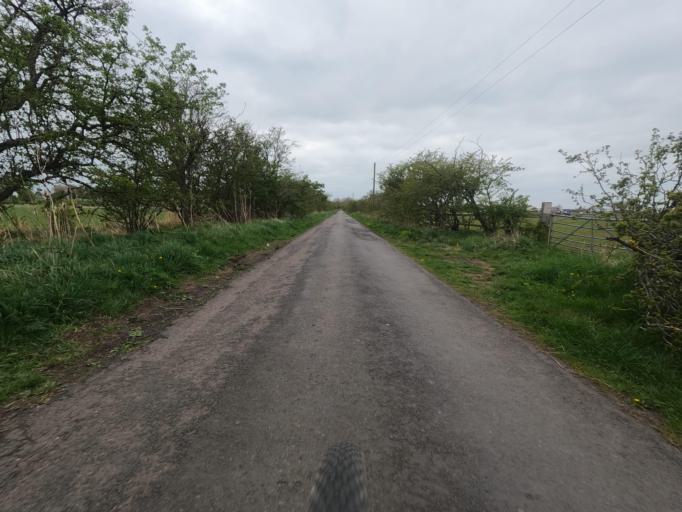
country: GB
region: England
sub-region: Northumberland
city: Ponteland
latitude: 55.0563
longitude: -1.7182
